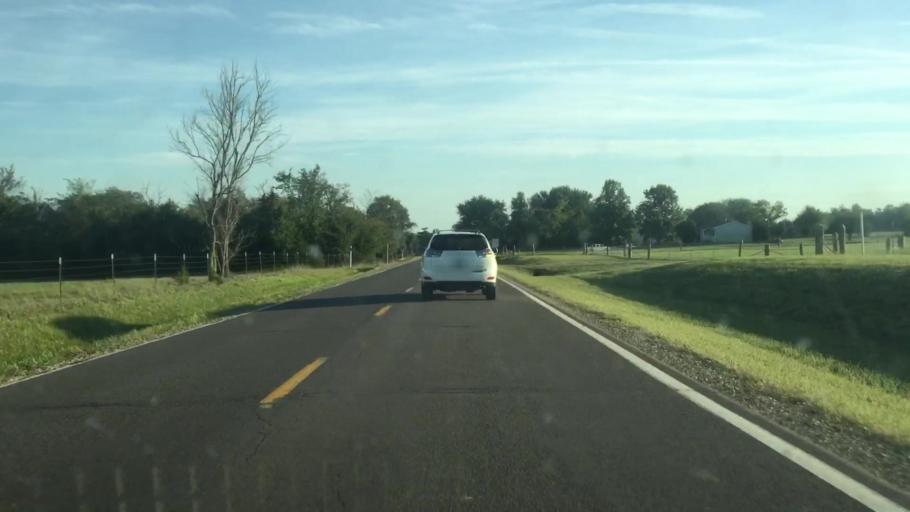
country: US
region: Kansas
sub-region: Brown County
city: Horton
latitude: 39.5589
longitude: -95.5247
